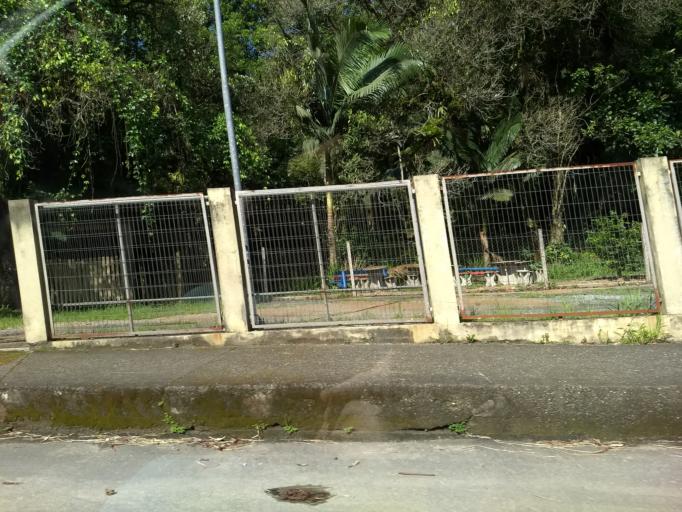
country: BR
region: Santa Catarina
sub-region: Schroeder
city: Schroeder
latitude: -26.4432
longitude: -49.1077
